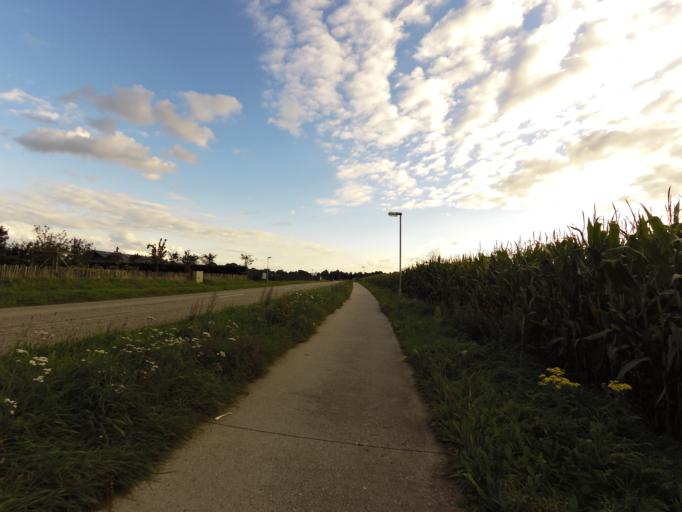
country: NL
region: Gelderland
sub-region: Gemeente Montferland
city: s-Heerenberg
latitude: 51.9121
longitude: 6.2637
